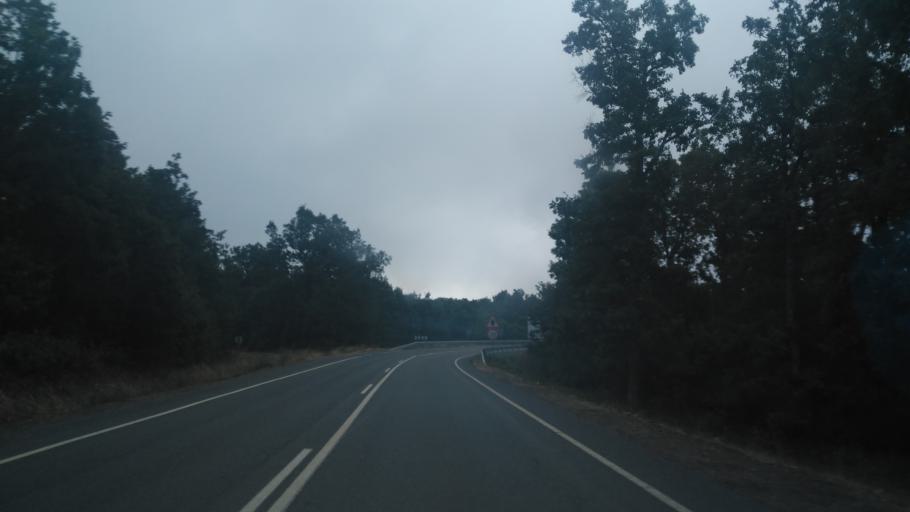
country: ES
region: Castille and Leon
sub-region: Provincia de Salamanca
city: Cilleros de la Bastida
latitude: 40.5592
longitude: -6.0679
